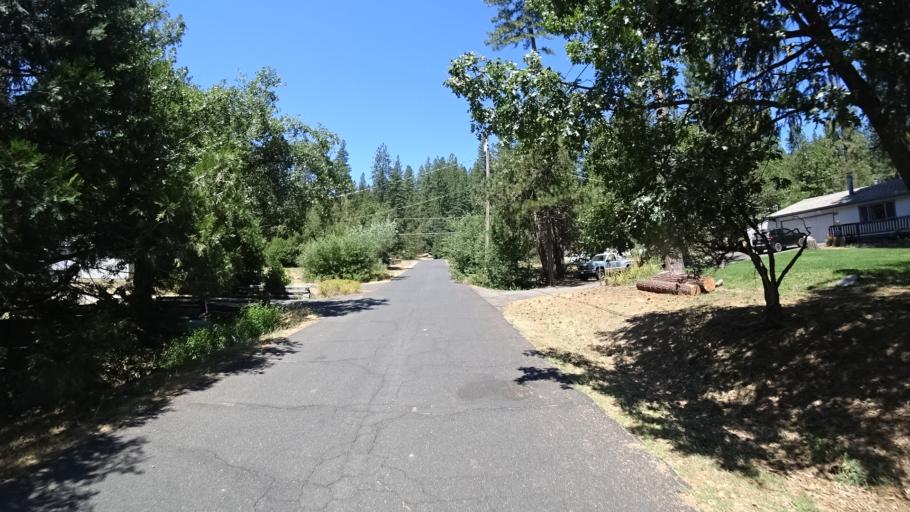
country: US
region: California
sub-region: Calaveras County
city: Forest Meadows
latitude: 38.2070
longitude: -120.3757
